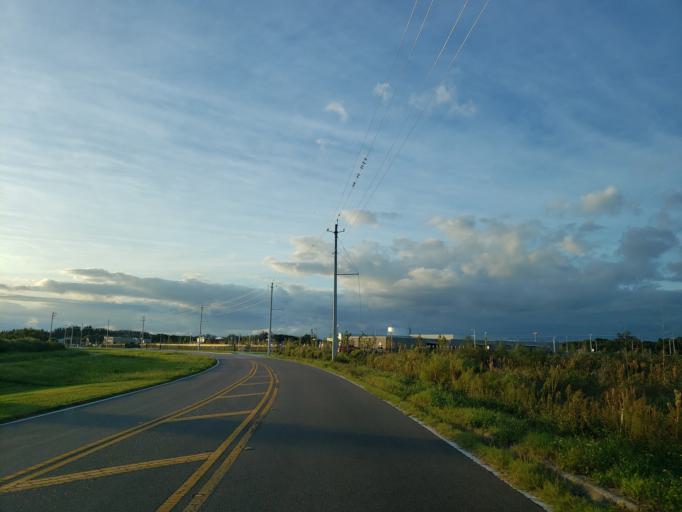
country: US
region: Florida
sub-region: Hillsborough County
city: Riverview
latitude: 27.7969
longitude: -82.3298
